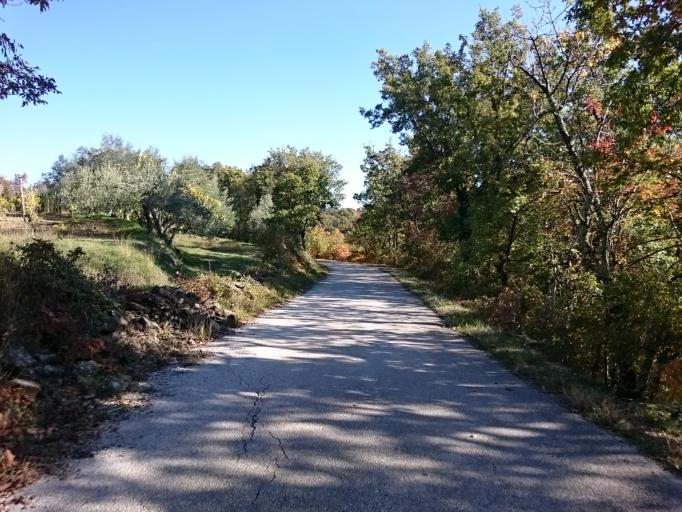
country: HR
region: Istarska
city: Buje
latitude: 45.4311
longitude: 13.7392
